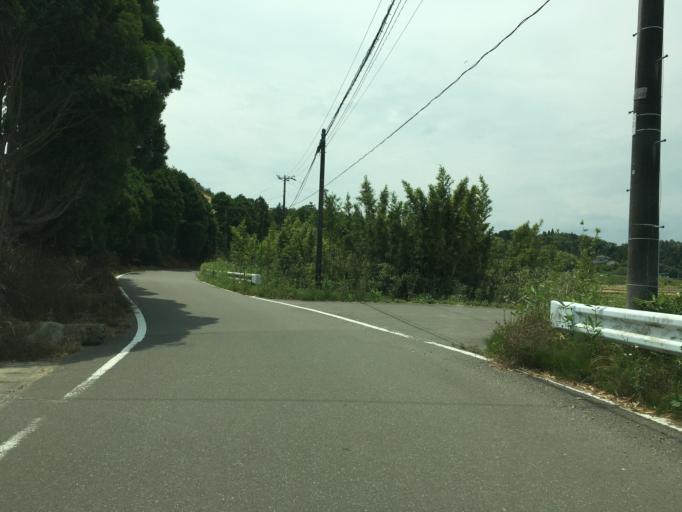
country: JP
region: Fukushima
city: Namie
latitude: 37.7470
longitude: 140.9935
